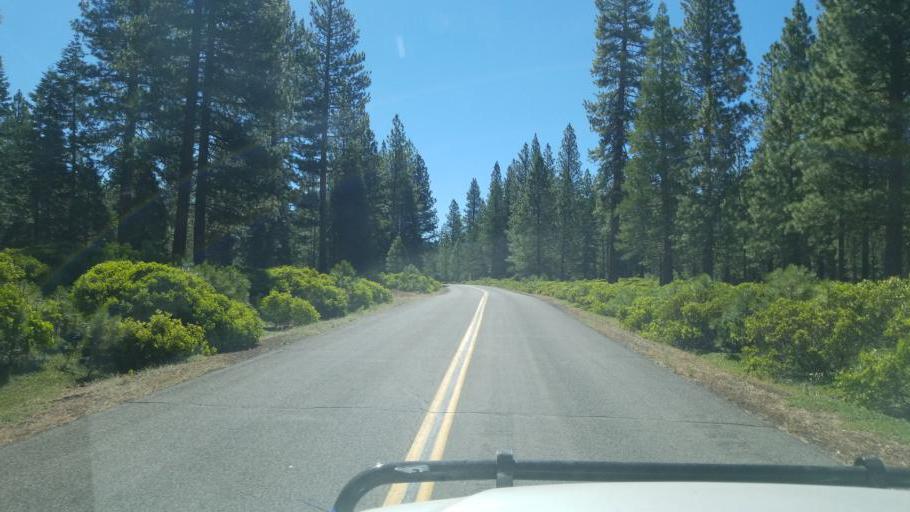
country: US
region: California
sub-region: Lassen County
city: Susanville
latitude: 40.5388
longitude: -120.7887
